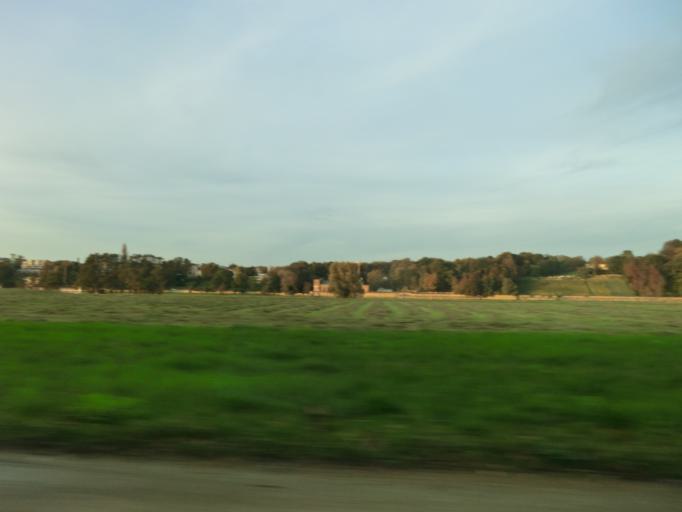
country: DE
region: Saxony
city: Albertstadt
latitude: 51.0601
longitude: 13.7877
